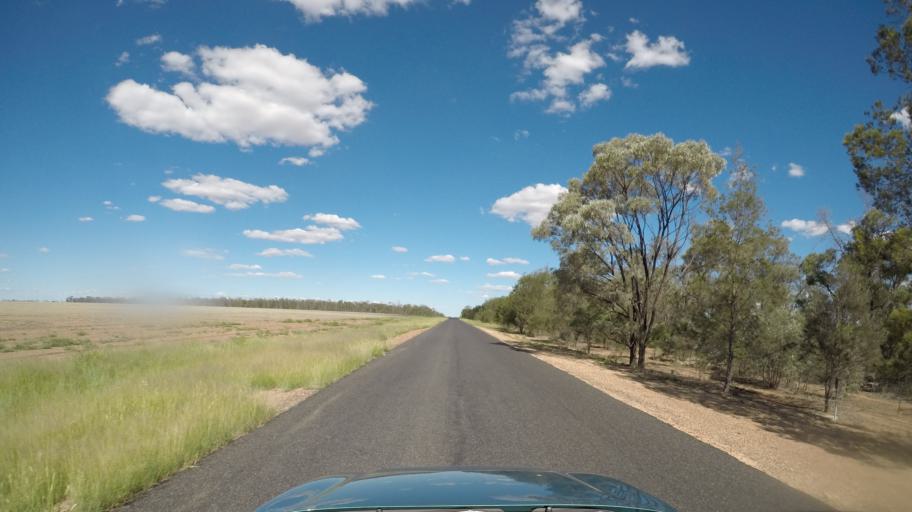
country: AU
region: Queensland
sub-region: Goondiwindi
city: Goondiwindi
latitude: -28.1720
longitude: 150.2267
